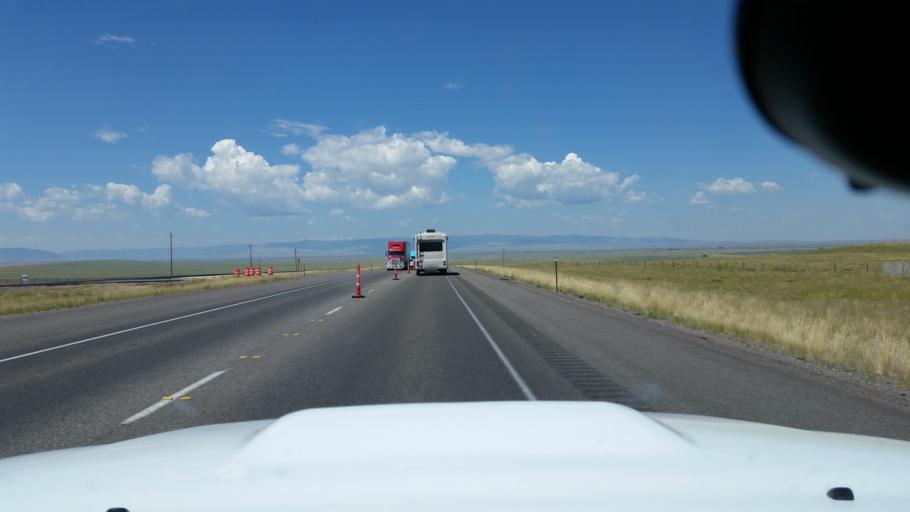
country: US
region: Wyoming
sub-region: Albany County
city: Laramie
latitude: 41.3495
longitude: -105.7061
